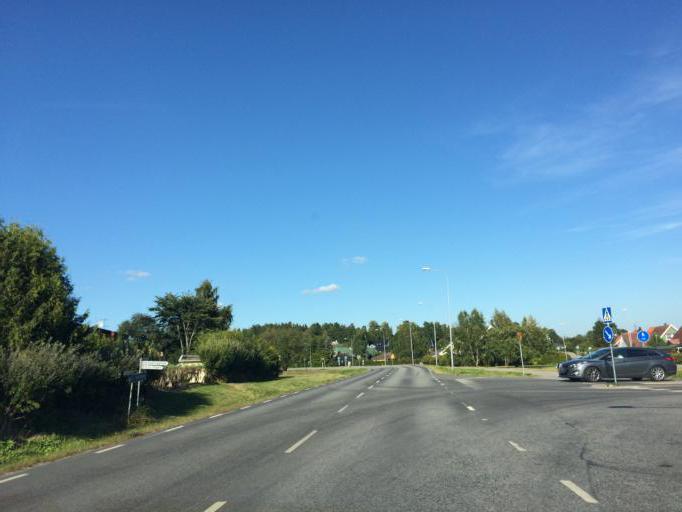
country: SE
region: Stockholm
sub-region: Upplands Vasby Kommun
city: Upplands Vaesby
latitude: 59.4951
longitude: 17.9500
